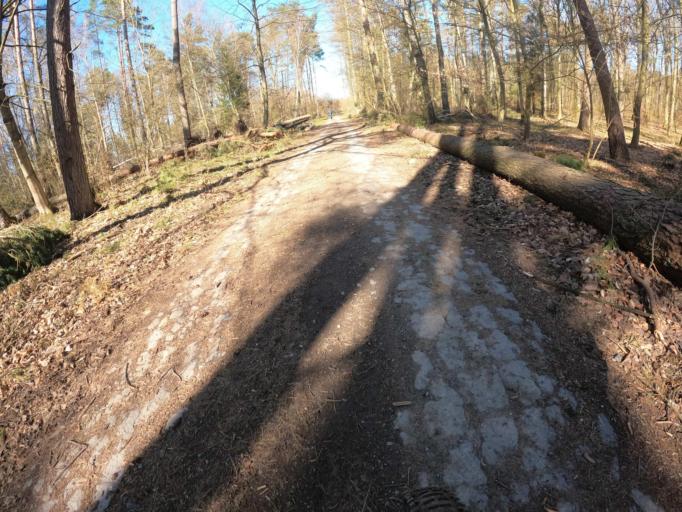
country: PL
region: West Pomeranian Voivodeship
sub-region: Powiat gryficki
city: Brojce
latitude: 54.0107
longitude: 15.3989
